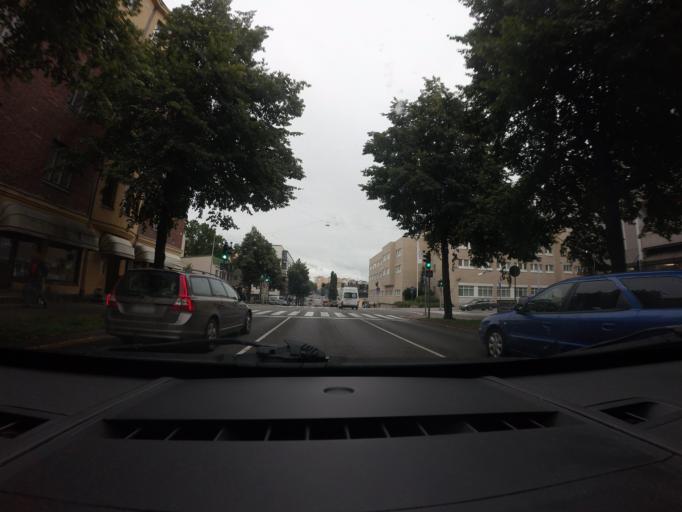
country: FI
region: Varsinais-Suomi
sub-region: Turku
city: Turku
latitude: 60.4463
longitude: 22.2530
